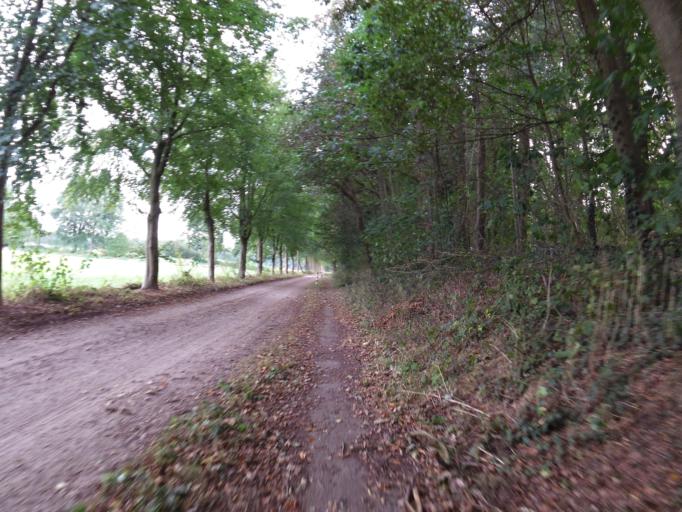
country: NL
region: North Brabant
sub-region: Gemeente Vught
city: Vught
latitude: 51.6646
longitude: 5.2430
